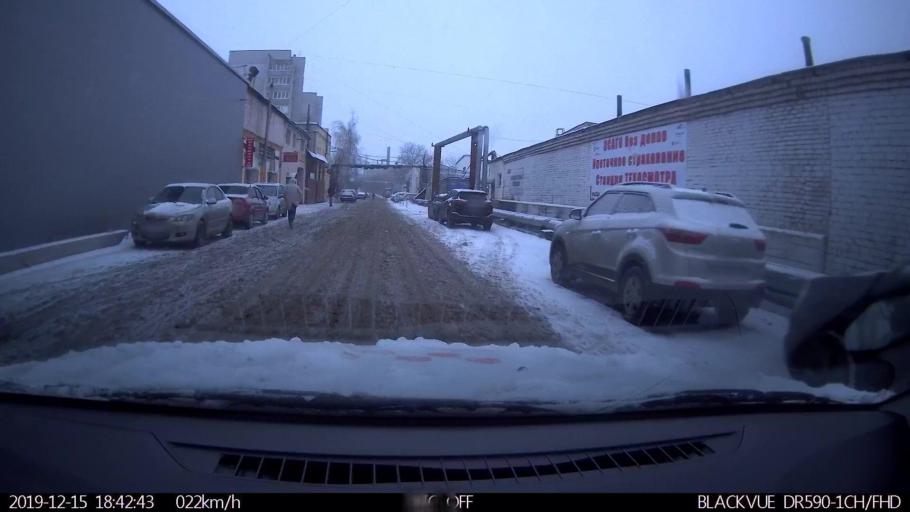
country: RU
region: Nizjnij Novgorod
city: Nizhniy Novgorod
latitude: 56.3256
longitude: 43.9226
